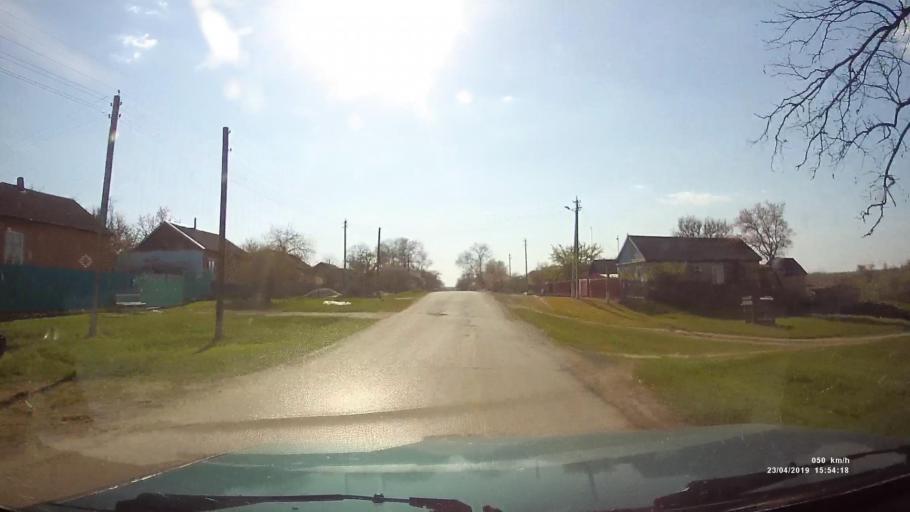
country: RU
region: Rostov
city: Remontnoye
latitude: 46.5368
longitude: 43.1285
